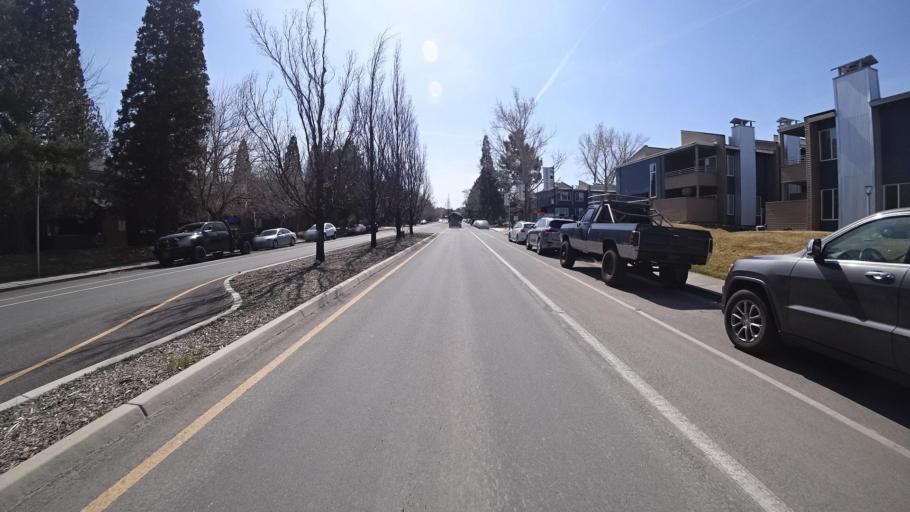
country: US
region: Nevada
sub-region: Washoe County
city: Reno
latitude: 39.4746
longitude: -119.8117
